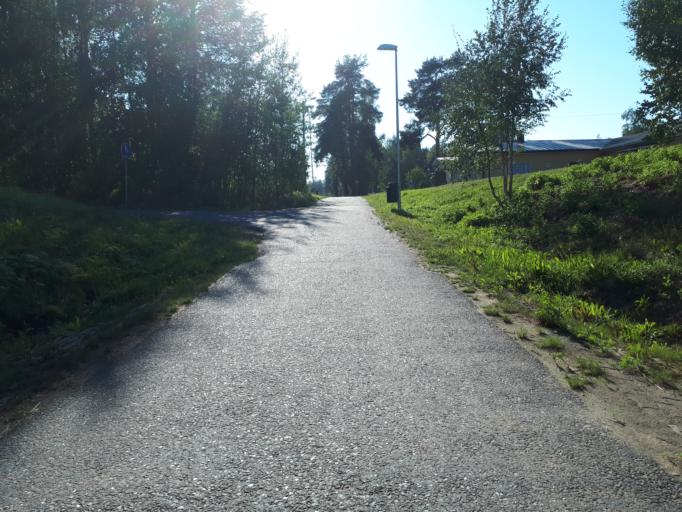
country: FI
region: Northern Ostrobothnia
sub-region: Oulunkaari
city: Ii
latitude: 65.3245
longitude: 25.3801
